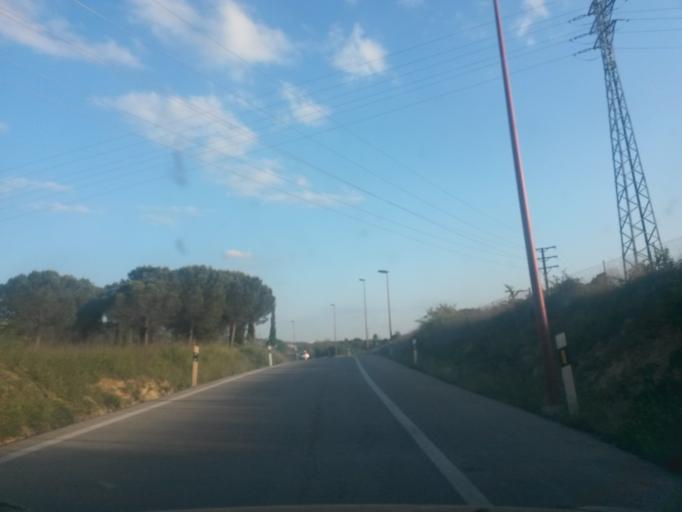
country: ES
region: Catalonia
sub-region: Provincia de Girona
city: Sarria de Ter
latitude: 42.0328
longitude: 2.8251
